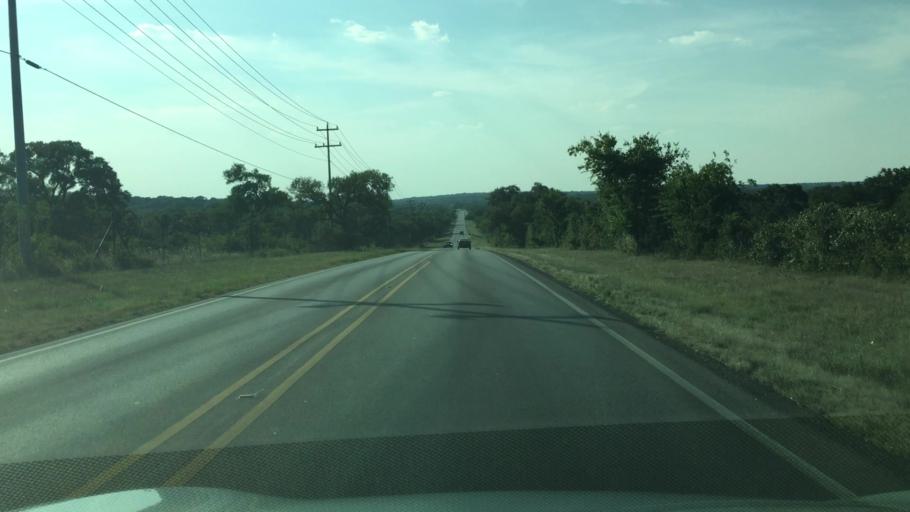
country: US
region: Texas
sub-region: Travis County
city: Shady Hollow
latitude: 30.1032
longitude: -97.9397
